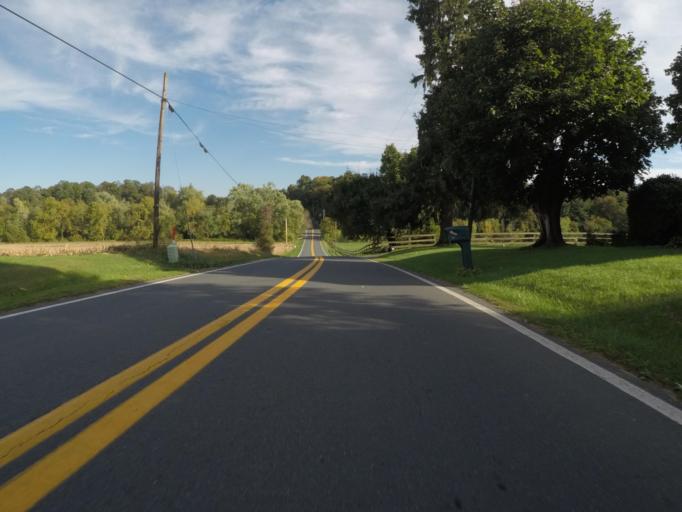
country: US
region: Maryland
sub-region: Carroll County
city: Hampstead
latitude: 39.5613
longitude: -76.8500
